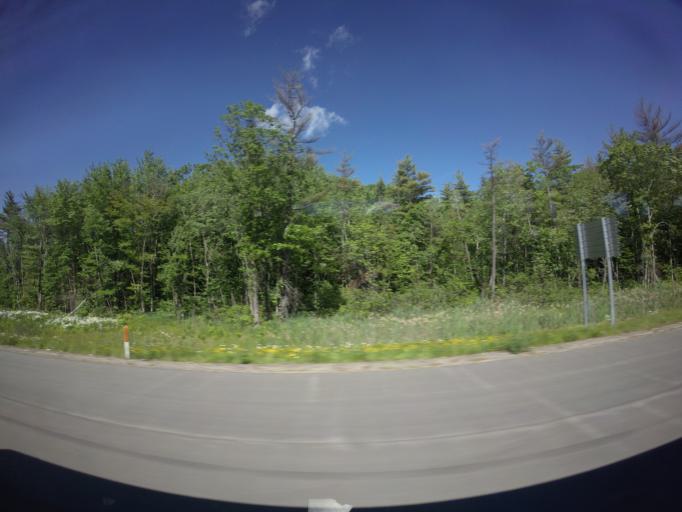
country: US
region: New Hampshire
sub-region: Rockingham County
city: Londonderry
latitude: 42.9274
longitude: -71.3783
